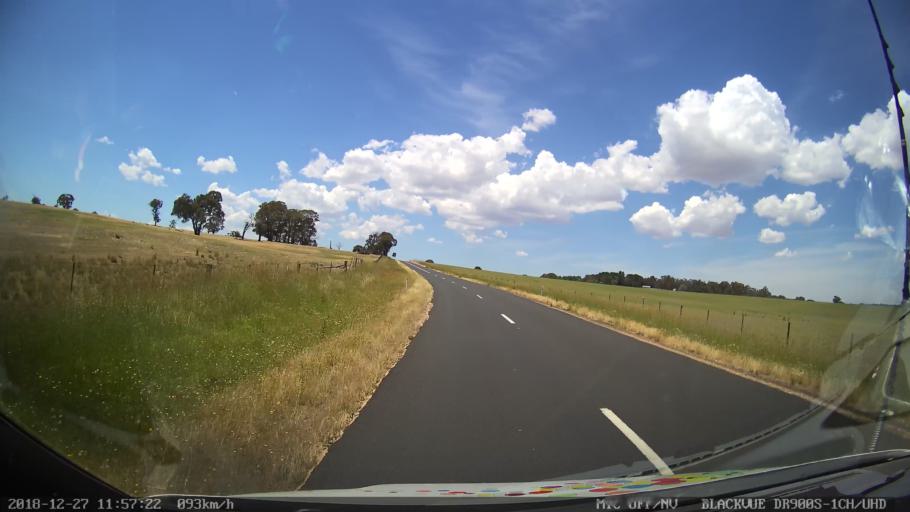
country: AU
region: New South Wales
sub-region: Blayney
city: Blayney
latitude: -33.7108
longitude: 149.3866
